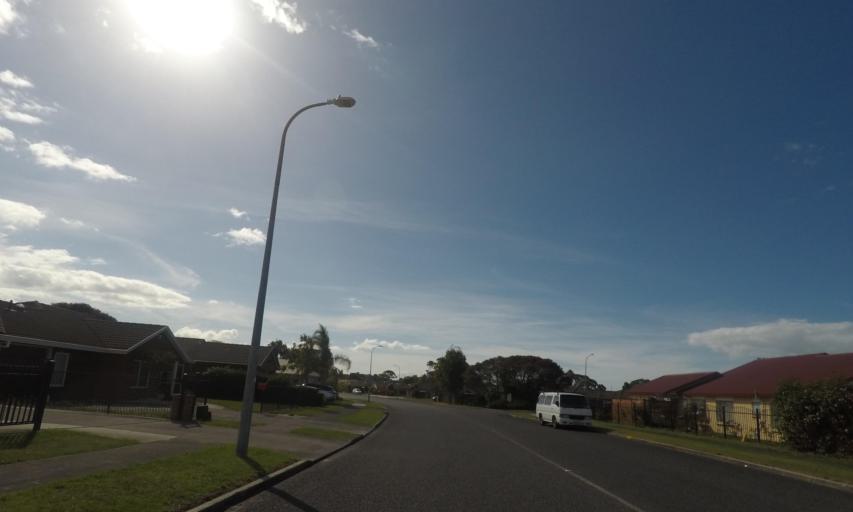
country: NZ
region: Auckland
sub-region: Auckland
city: Pakuranga
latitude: -36.9234
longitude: 174.9001
